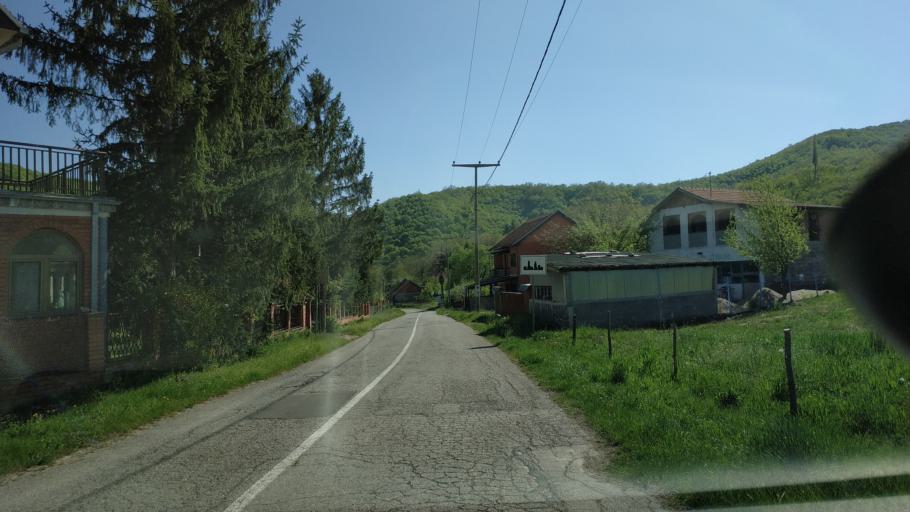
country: RS
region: Central Serbia
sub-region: Nisavski Okrug
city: Nis
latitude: 43.4270
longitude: 21.8498
